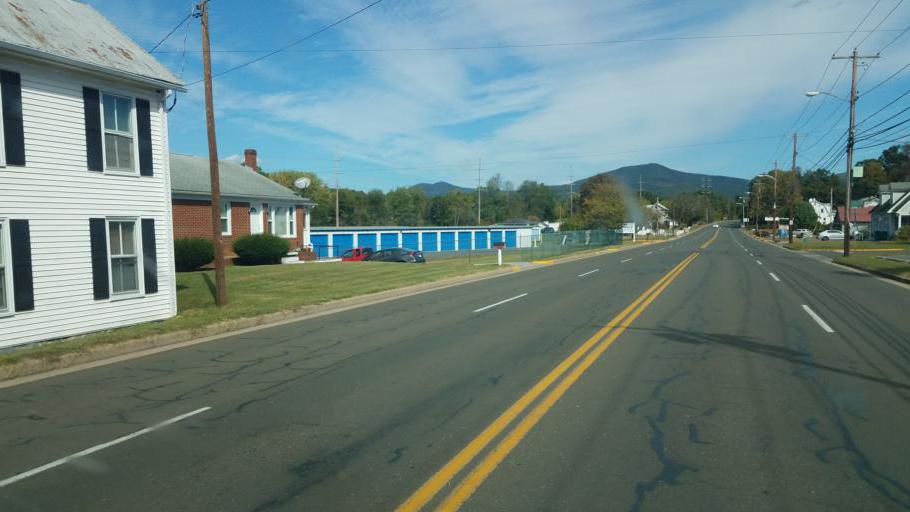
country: US
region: Virginia
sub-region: Page County
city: Luray
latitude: 38.6685
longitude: -78.4374
